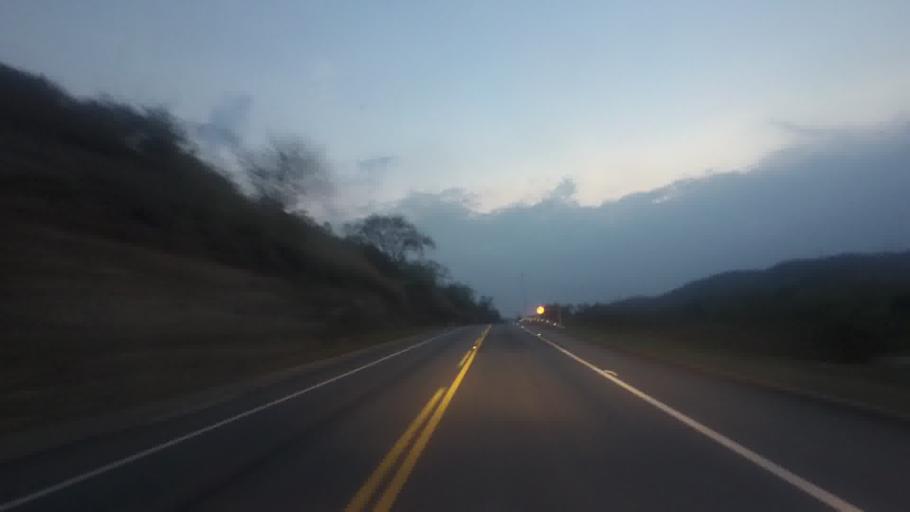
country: BR
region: Minas Gerais
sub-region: Alem Paraiba
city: Alem Paraiba
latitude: -21.9269
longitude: -42.7797
